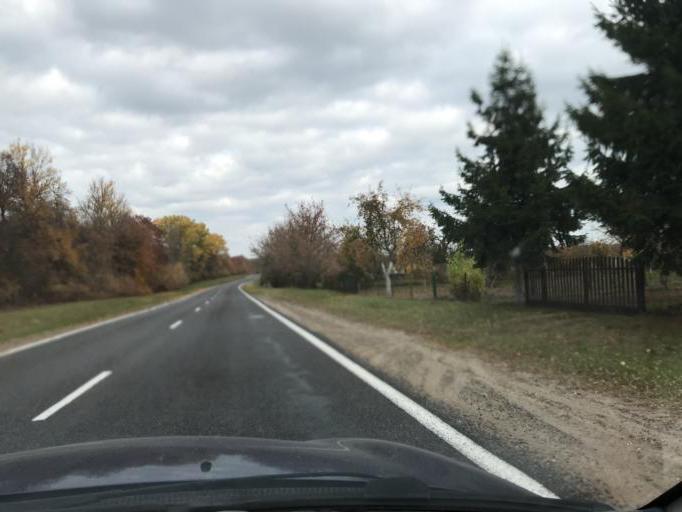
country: BY
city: Berezovka
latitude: 53.7426
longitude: 25.3755
